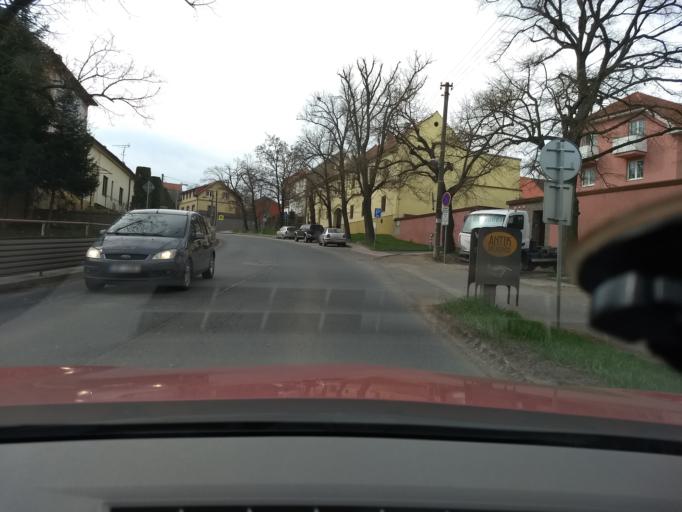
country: CZ
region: Central Bohemia
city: Horomerice
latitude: 50.1345
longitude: 14.3363
